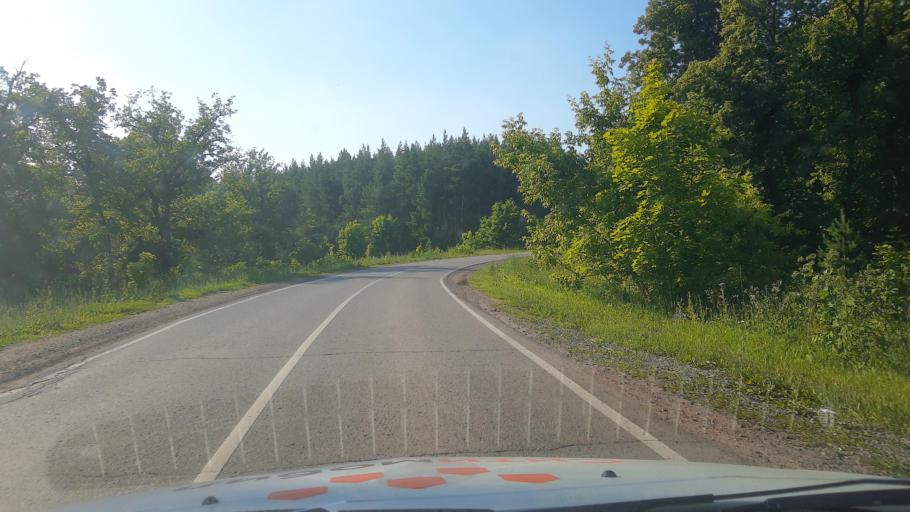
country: RU
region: Bashkortostan
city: Avdon
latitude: 54.6263
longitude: 55.6264
